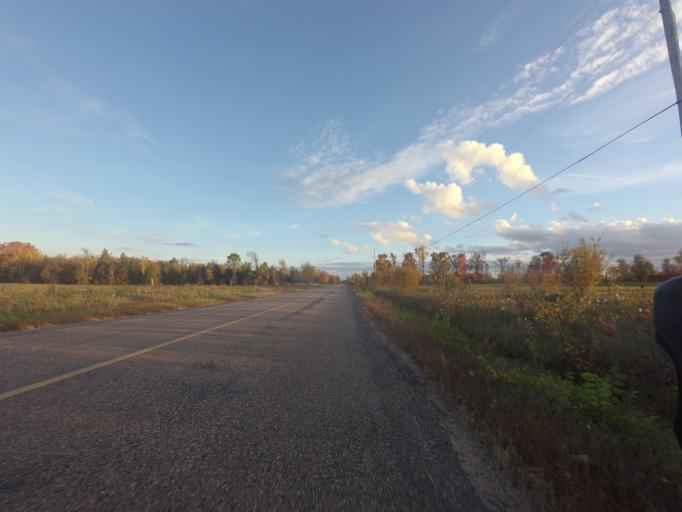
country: CA
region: Ontario
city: Renfrew
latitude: 45.4460
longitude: -76.9677
